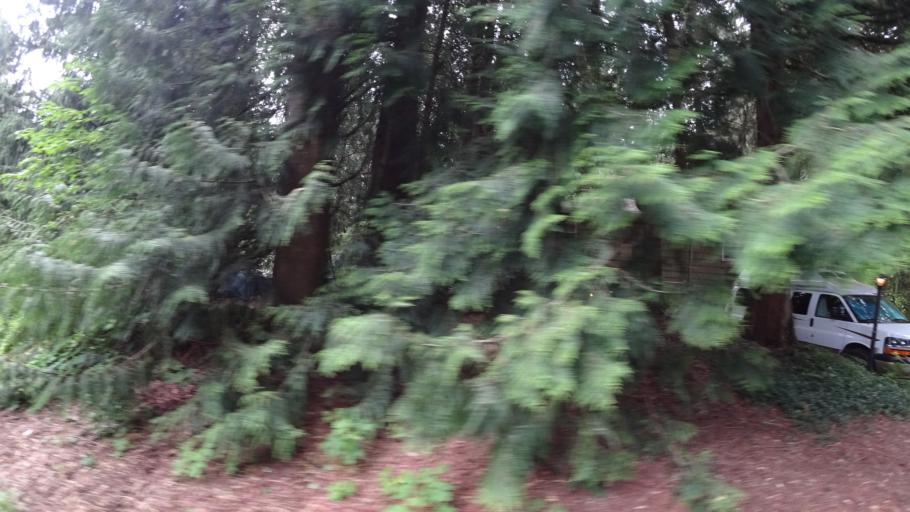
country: US
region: Oregon
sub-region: Washington County
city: Garden Home-Whitford
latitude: 45.4698
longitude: -122.7449
